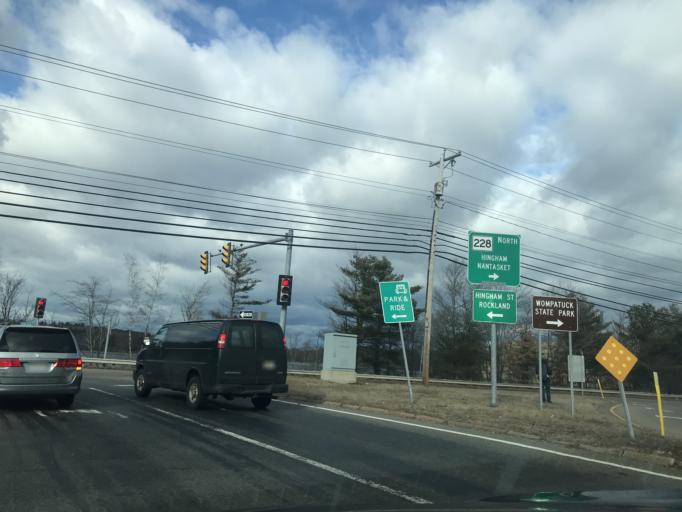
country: US
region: Massachusetts
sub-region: Plymouth County
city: Rockland
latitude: 42.1666
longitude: -70.8900
